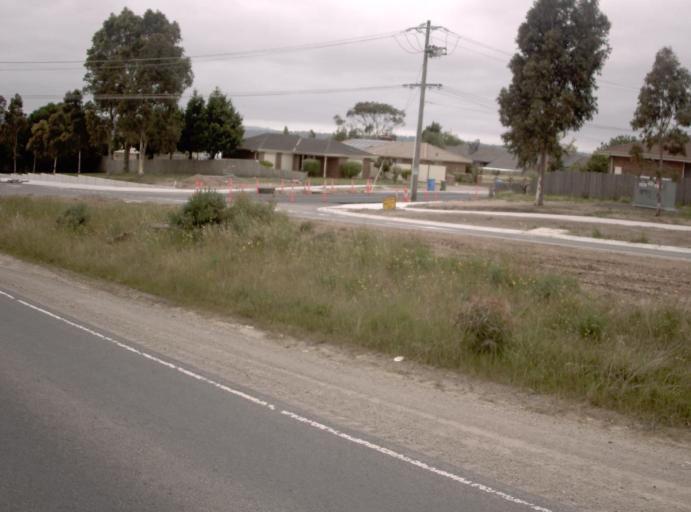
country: AU
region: Victoria
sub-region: Casey
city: Lynbrook
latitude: -38.0424
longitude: 145.2658
